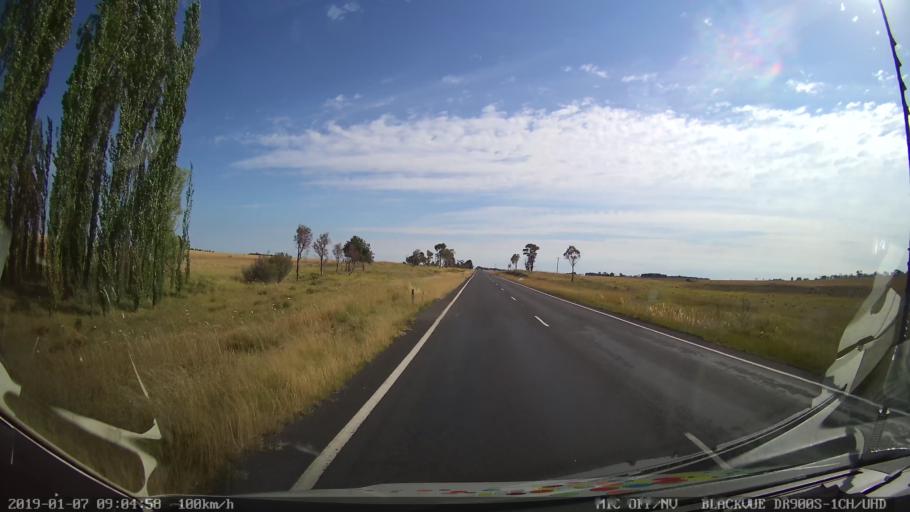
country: AU
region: New South Wales
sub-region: Armidale Dumaresq
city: Armidale
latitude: -30.7152
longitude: 151.4575
